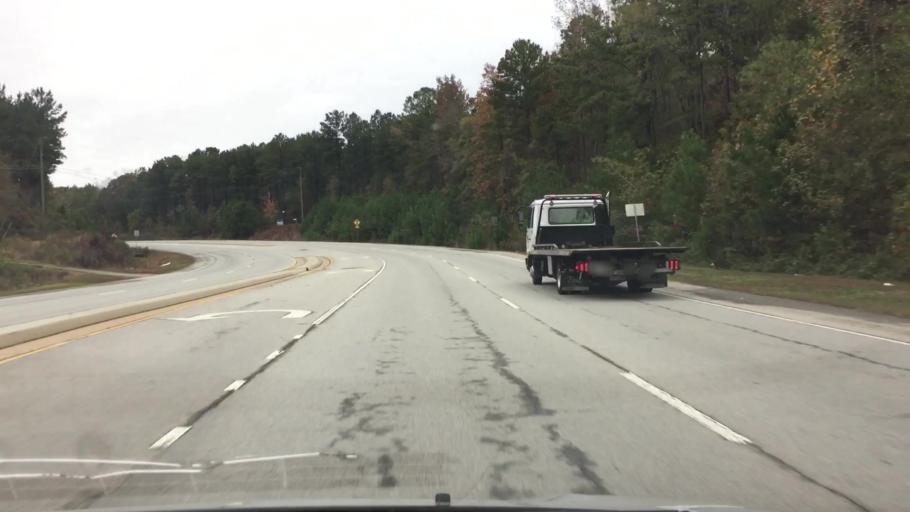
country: US
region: Georgia
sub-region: Henry County
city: McDonough
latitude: 33.5189
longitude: -84.1634
